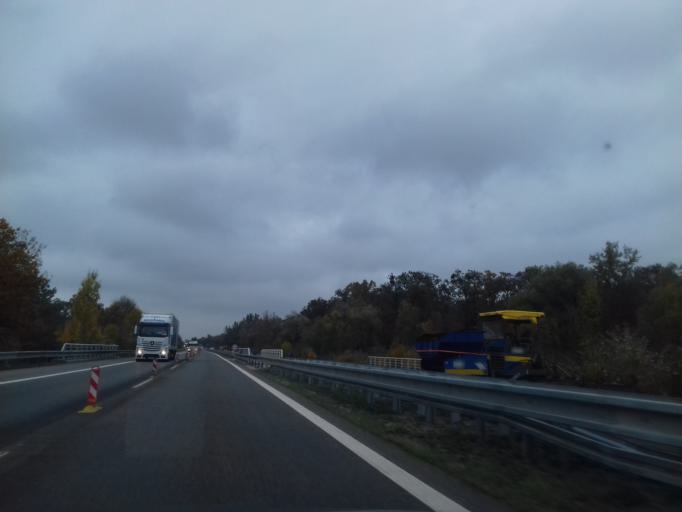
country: CZ
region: South Moravian
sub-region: Okres Breclav
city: Lanzhot
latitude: 48.7105
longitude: 16.9867
